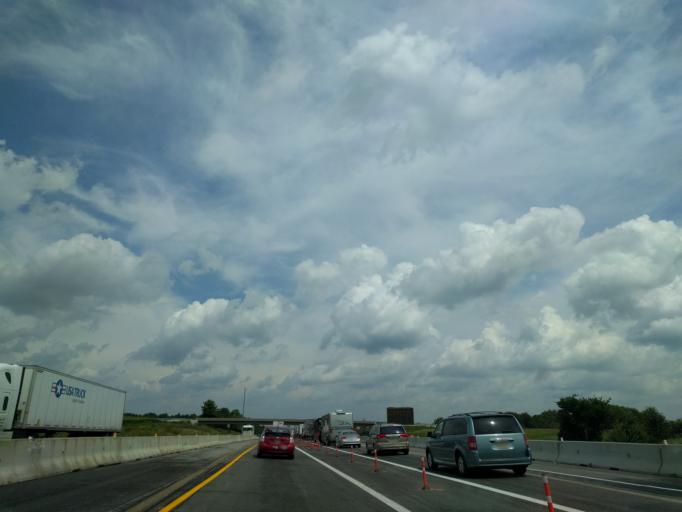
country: US
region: Kentucky
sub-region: Larue County
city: Hodgenville
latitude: 37.5514
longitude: -85.8785
